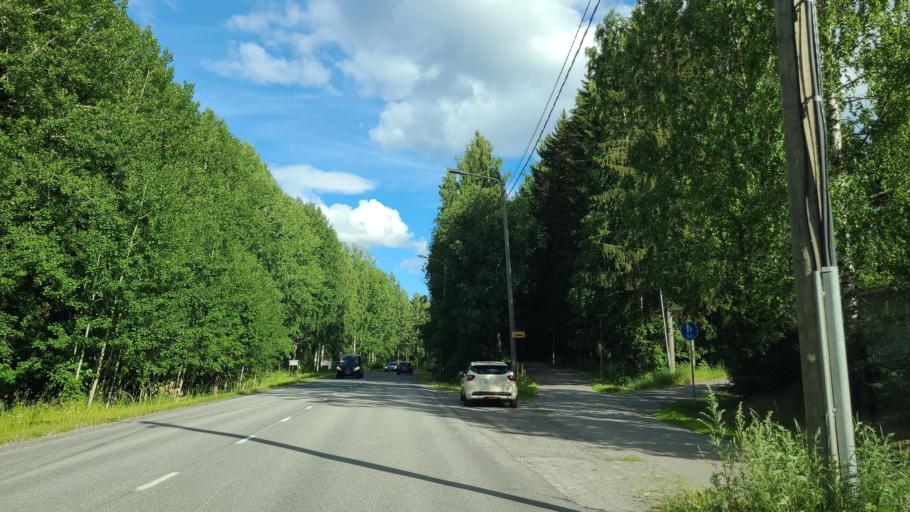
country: FI
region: Northern Savo
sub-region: Kuopio
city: Kuopio
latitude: 62.9359
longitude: 27.6616
